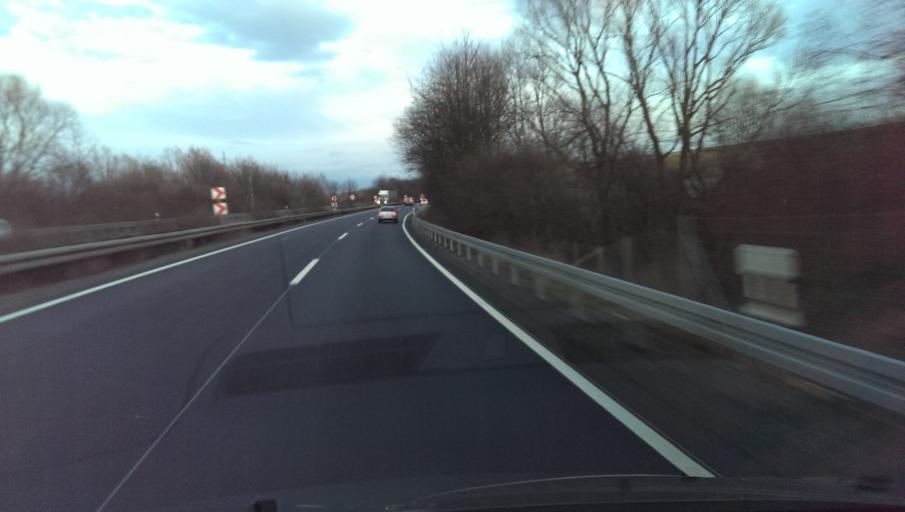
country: DE
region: Lower Saxony
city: Goslar
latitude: 51.9318
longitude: 10.4850
